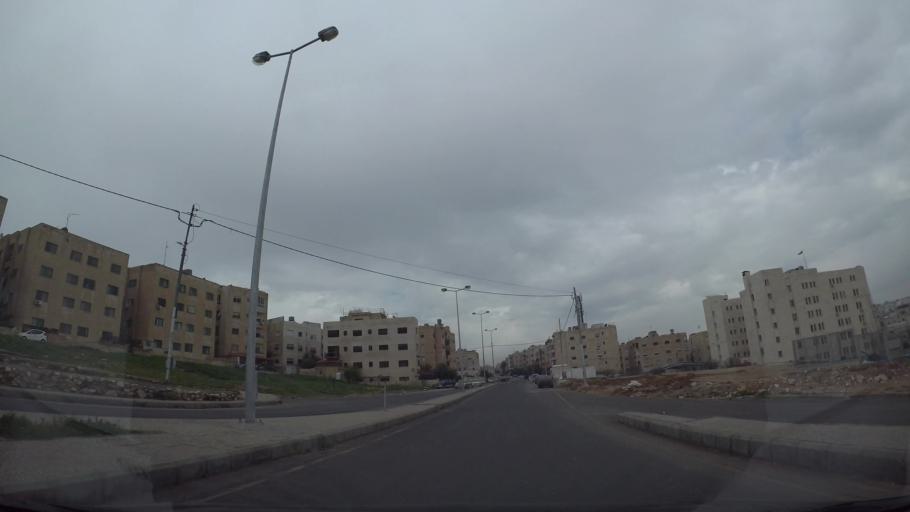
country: JO
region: Amman
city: Amman
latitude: 31.9818
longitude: 35.9310
